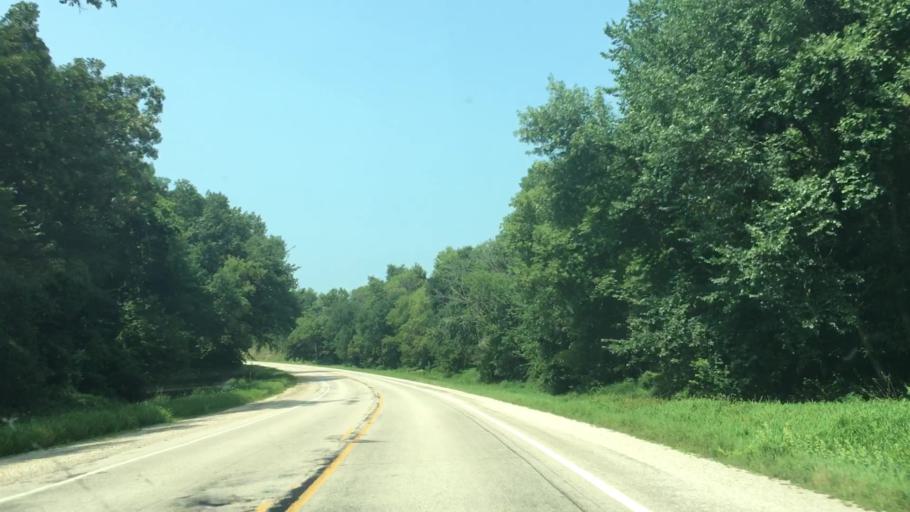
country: US
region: Iowa
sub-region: Fayette County
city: West Union
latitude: 43.0769
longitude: -91.8396
